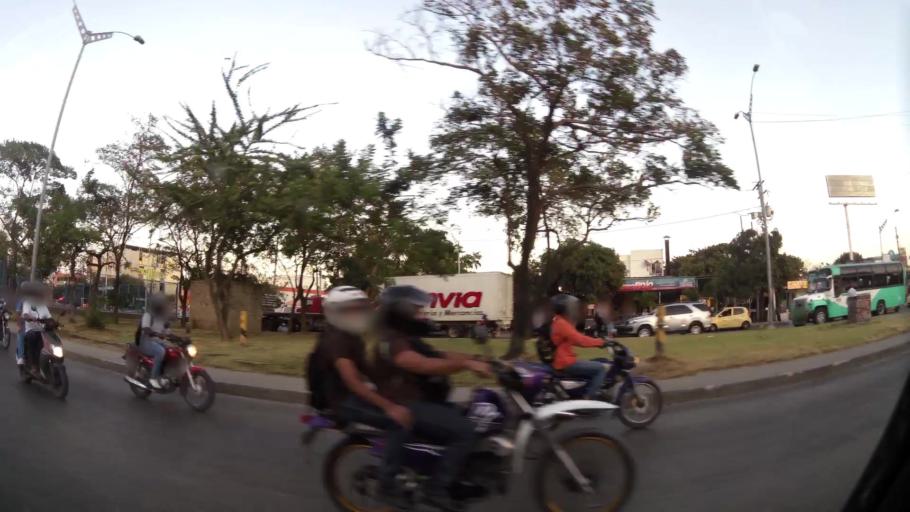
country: CO
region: Atlantico
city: Soledad
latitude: 10.9357
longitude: -74.7806
